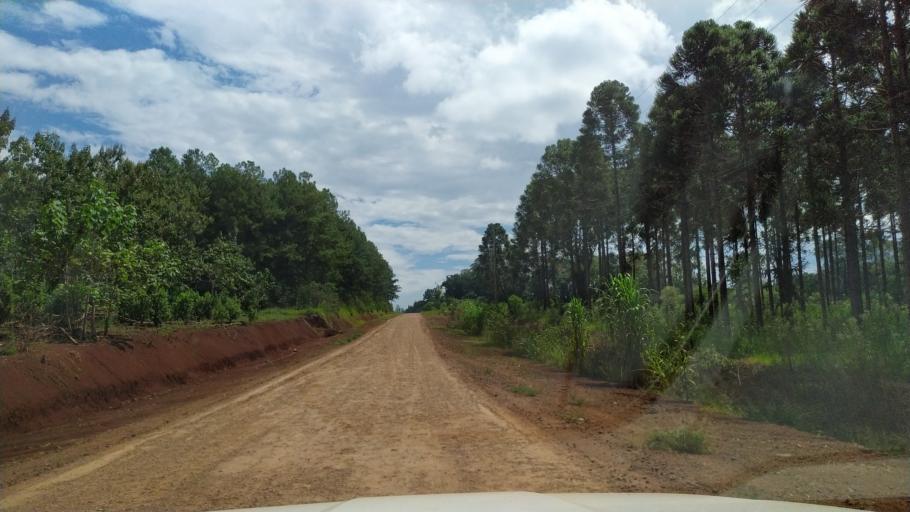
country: AR
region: Misiones
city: Puerto Piray
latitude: -26.5352
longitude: -54.6564
